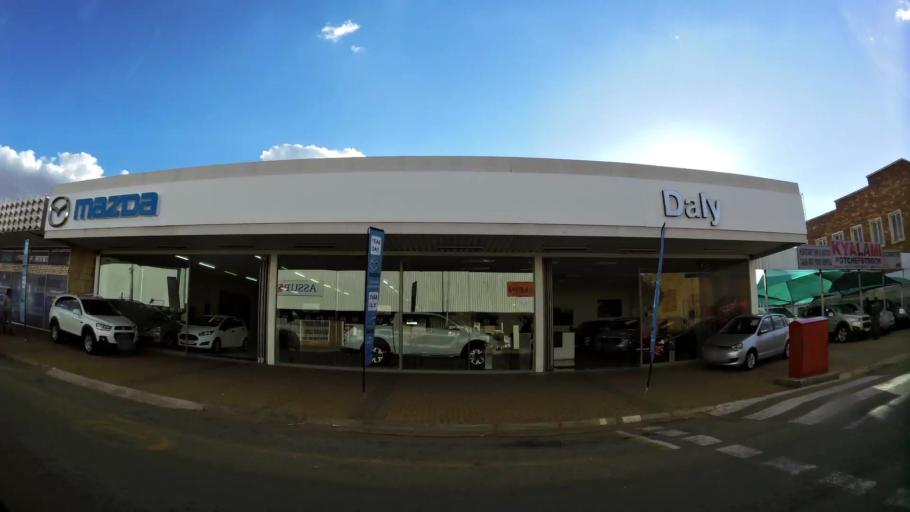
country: ZA
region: North-West
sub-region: Dr Kenneth Kaunda District Municipality
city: Potchefstroom
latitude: -26.7096
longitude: 27.0975
